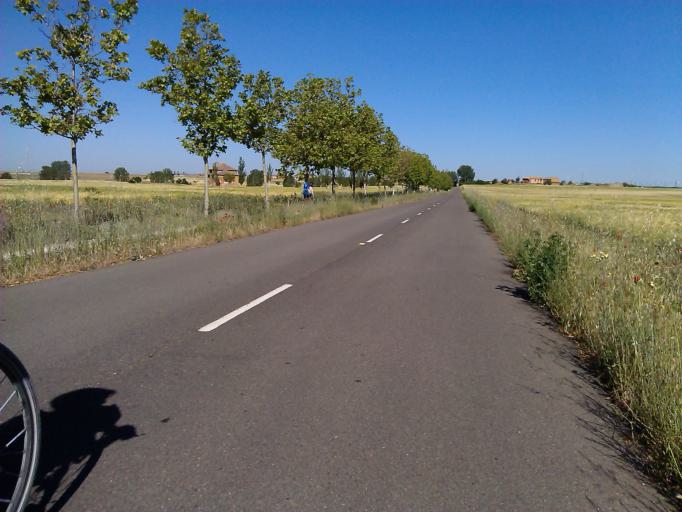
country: ES
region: Castille and Leon
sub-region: Provincia de Leon
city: Bercianos del Real Camino
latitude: 42.3876
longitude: -5.1229
